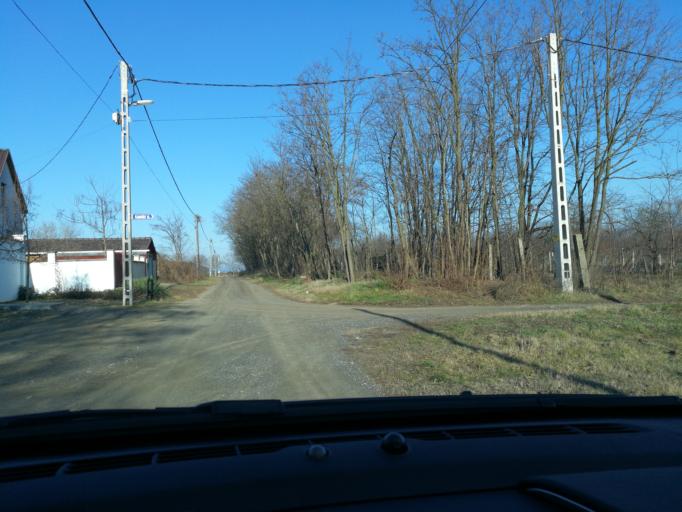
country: HU
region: Szabolcs-Szatmar-Bereg
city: Nyiregyhaza
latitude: 47.9712
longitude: 21.7573
